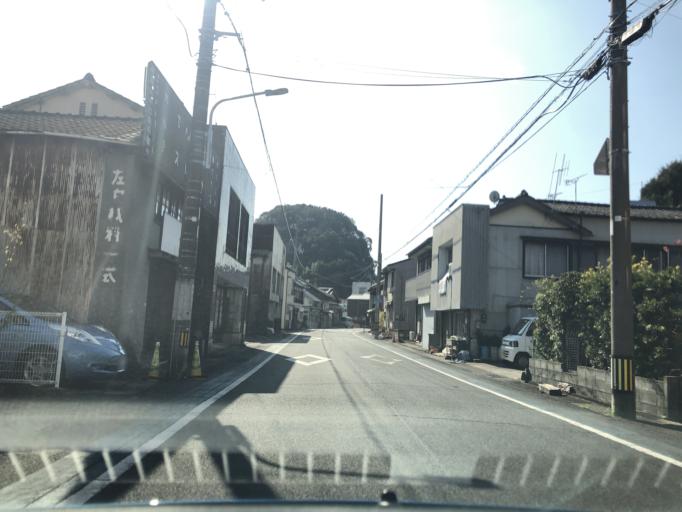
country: JP
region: Kochi
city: Sukumo
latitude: 32.9236
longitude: 132.7013
